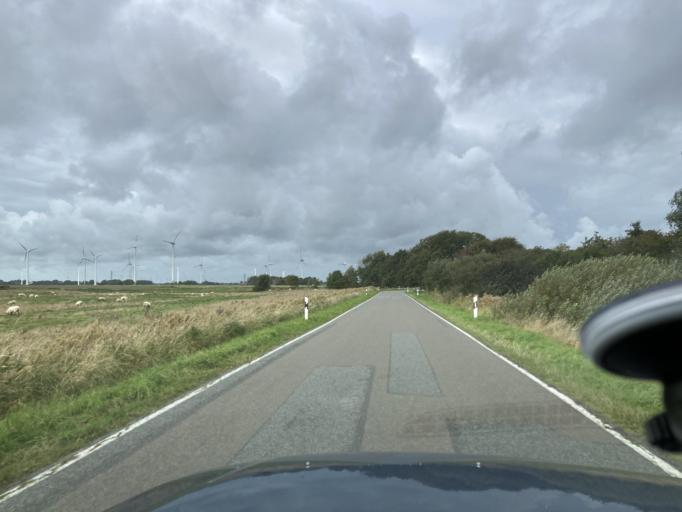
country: DE
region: Schleswig-Holstein
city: Wesselburener Deichhausen
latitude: 54.1730
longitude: 8.9319
